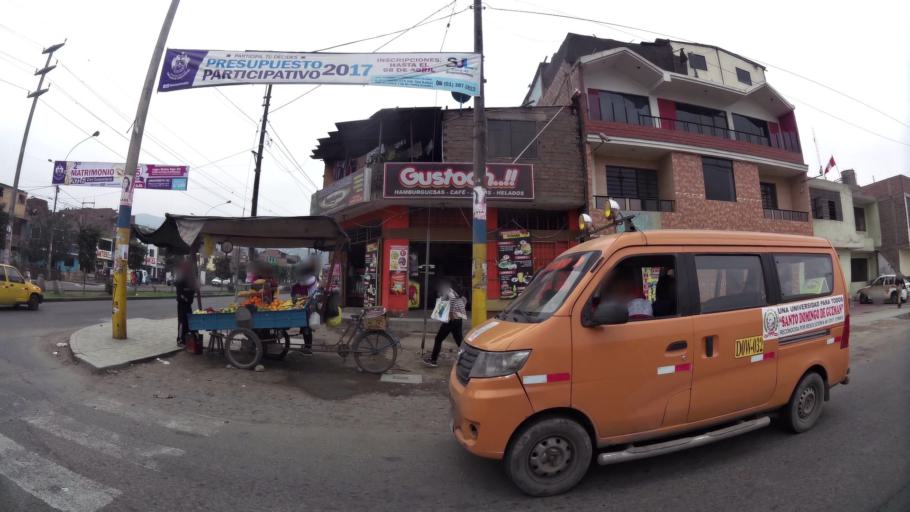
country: PE
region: Lima
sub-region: Lima
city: Independencia
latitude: -11.9629
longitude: -77.0007
